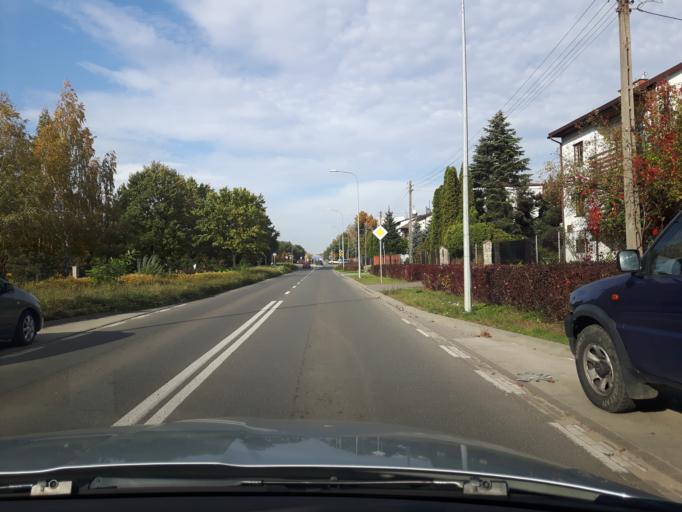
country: PL
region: Masovian Voivodeship
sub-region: Powiat wolominski
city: Zabki
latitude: 52.2953
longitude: 21.0972
